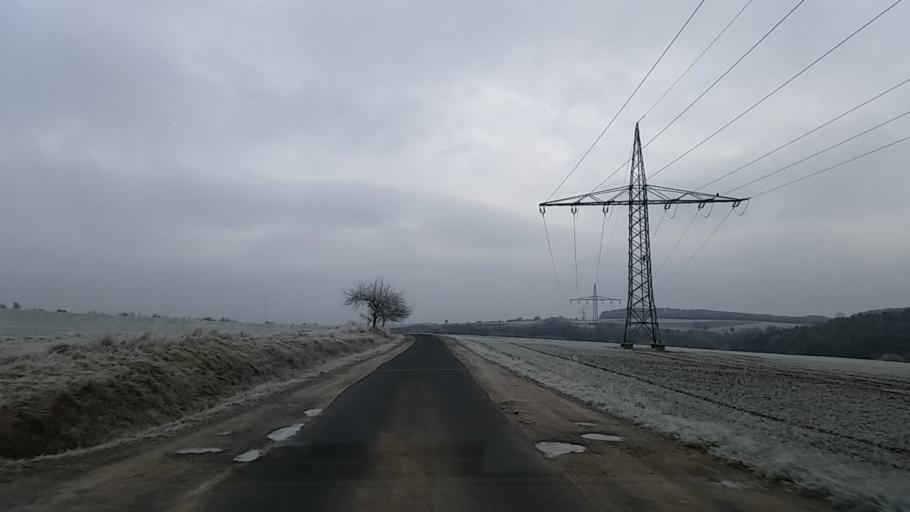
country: DE
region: Bavaria
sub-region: Regierungsbezirk Unterfranken
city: Fuchsstadt
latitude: 50.0363
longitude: 9.9037
